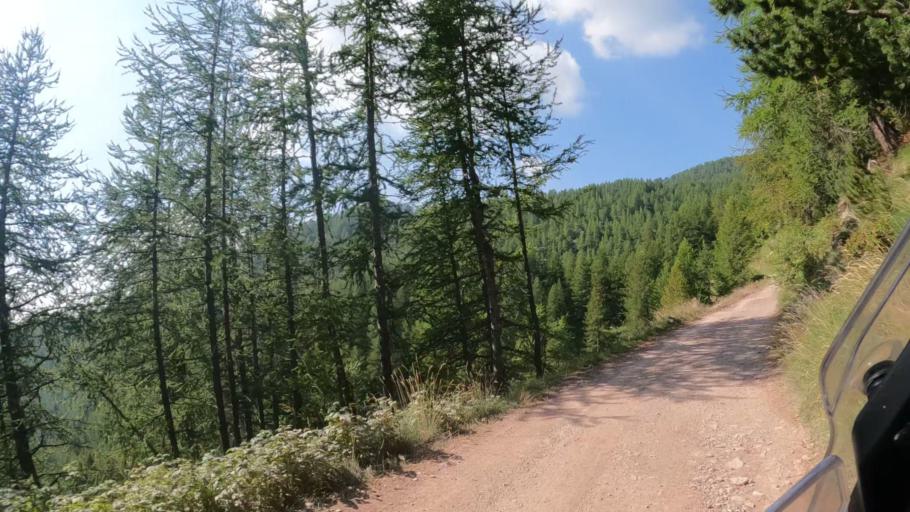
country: IT
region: Piedmont
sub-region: Provincia di Cuneo
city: Briga Alta
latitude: 44.1052
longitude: 7.7102
